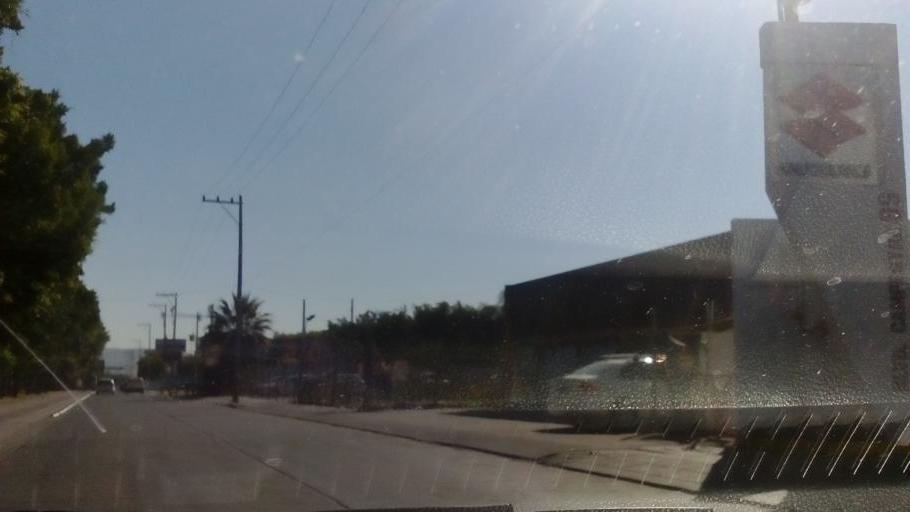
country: MX
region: Guanajuato
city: Leon
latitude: 21.1473
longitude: -101.6834
